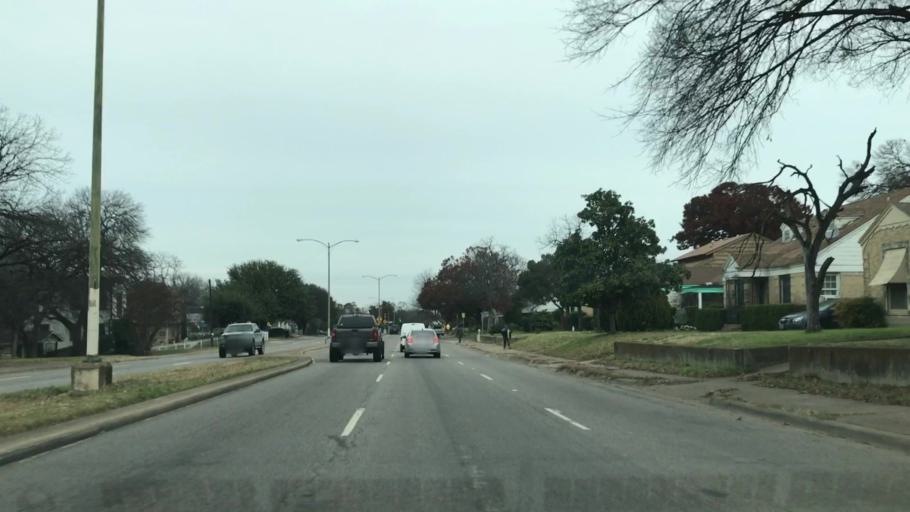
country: US
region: Texas
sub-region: Dallas County
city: Dallas
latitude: 32.7305
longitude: -96.8143
